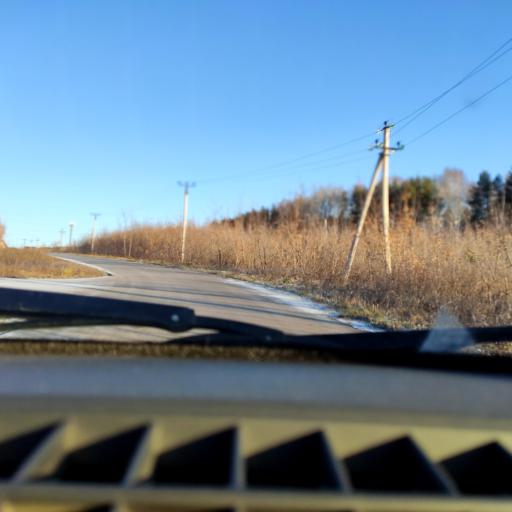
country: RU
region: Bashkortostan
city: Avdon
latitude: 54.6528
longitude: 55.7520
